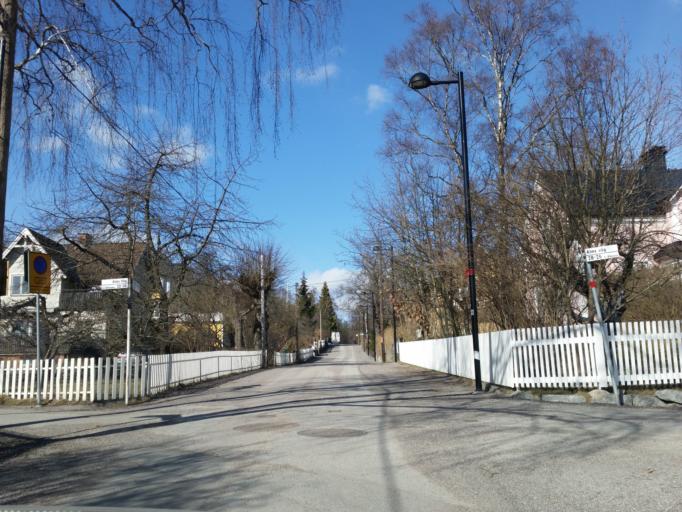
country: SE
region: Stockholm
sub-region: Sundbybergs Kommun
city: Sundbyberg
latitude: 59.3721
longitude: 17.9516
